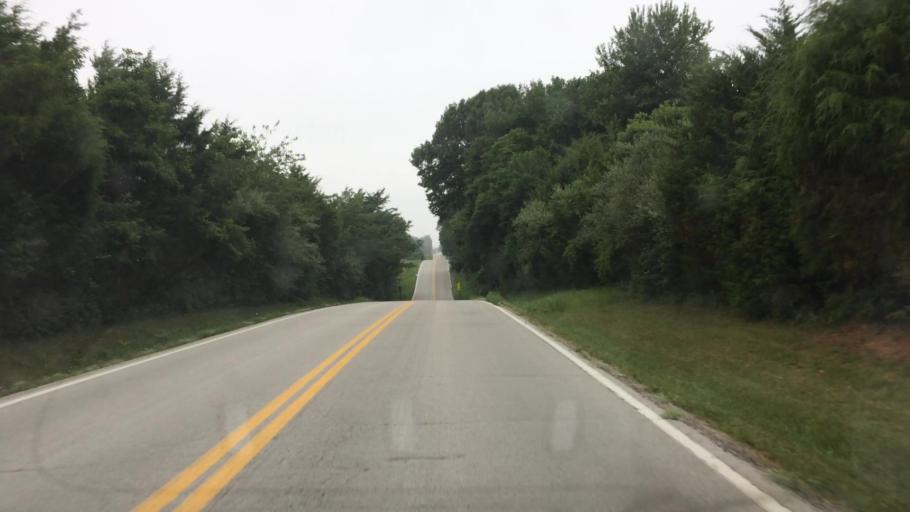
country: US
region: Missouri
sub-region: Greene County
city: Strafford
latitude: 37.2721
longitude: -93.1904
